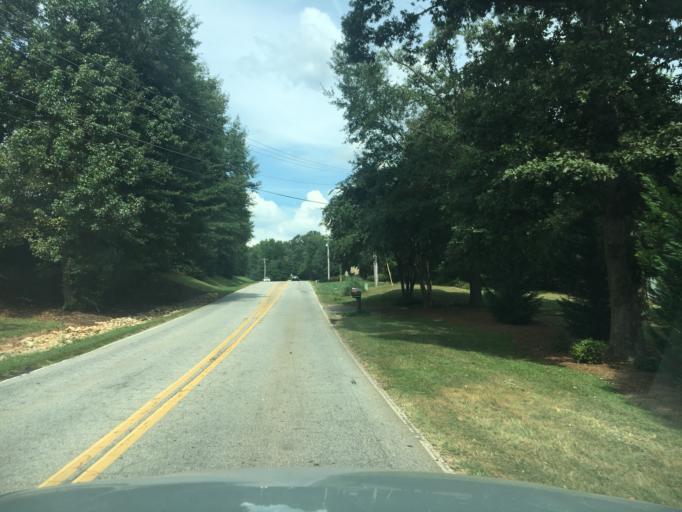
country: US
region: South Carolina
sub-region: Greenville County
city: Five Forks
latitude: 34.8146
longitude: -82.2306
